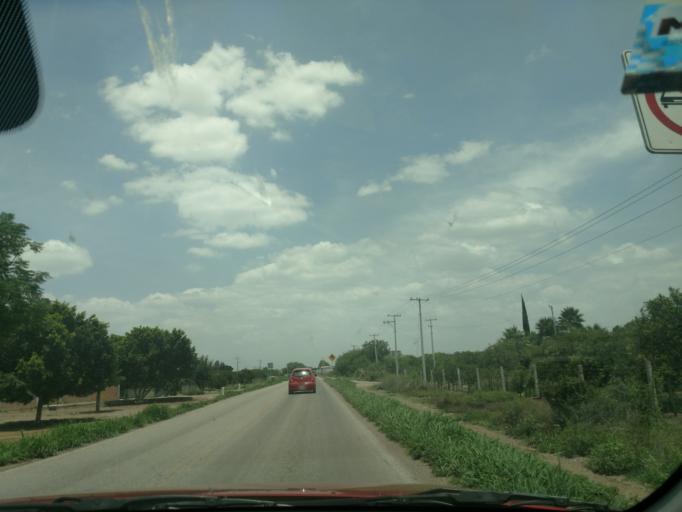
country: MX
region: San Luis Potosi
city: Ciudad Fernandez
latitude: 21.9520
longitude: -100.0658
